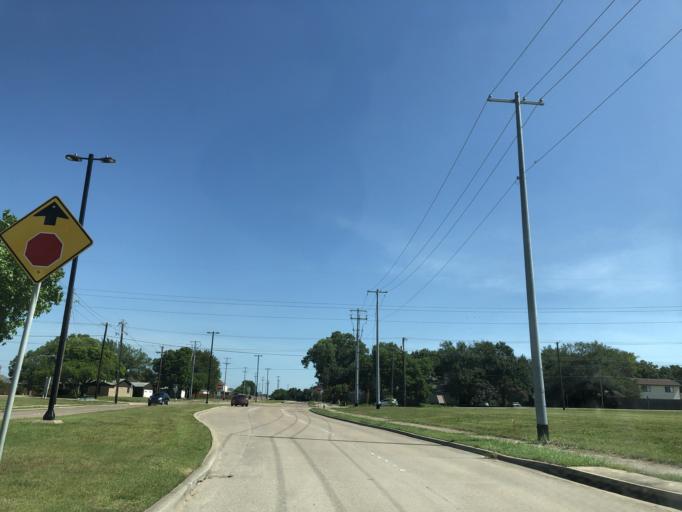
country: US
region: Texas
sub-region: Dallas County
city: Rowlett
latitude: 32.8501
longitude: -96.5826
